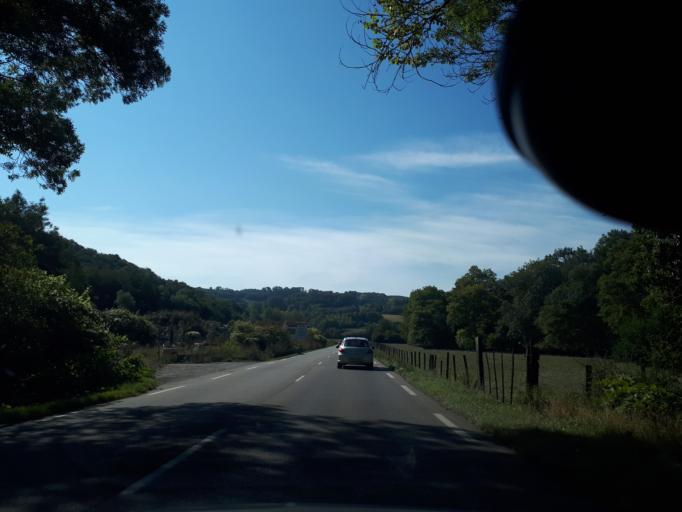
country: FR
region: Rhone-Alpes
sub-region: Departement de l'Isere
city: Maubec
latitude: 45.5596
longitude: 5.2749
